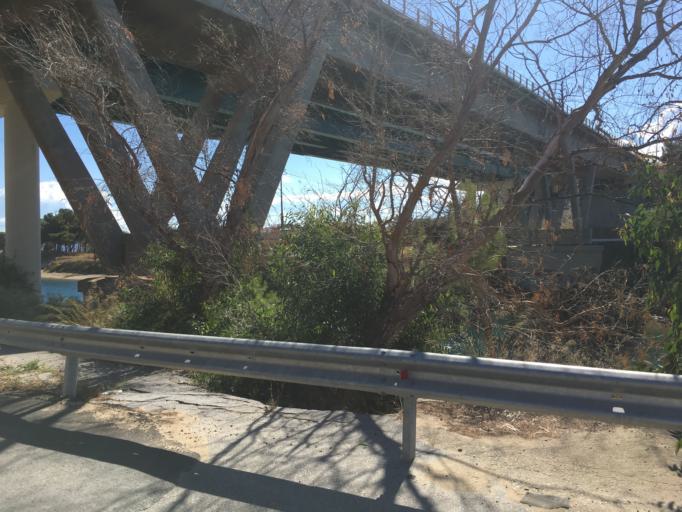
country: GR
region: Central Macedonia
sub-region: Nomos Chalkidikis
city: Nea Potidhaia
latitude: 40.1975
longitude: 23.3300
